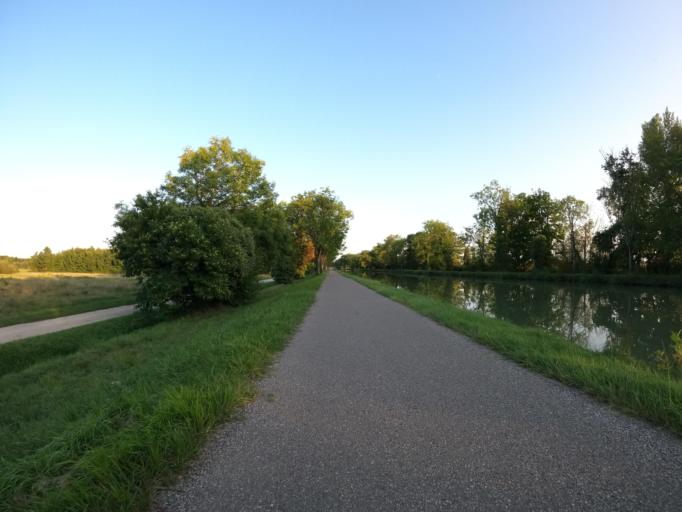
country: FR
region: Midi-Pyrenees
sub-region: Departement du Tarn-et-Garonne
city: Saint-Porquier
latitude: 43.9883
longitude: 1.2053
